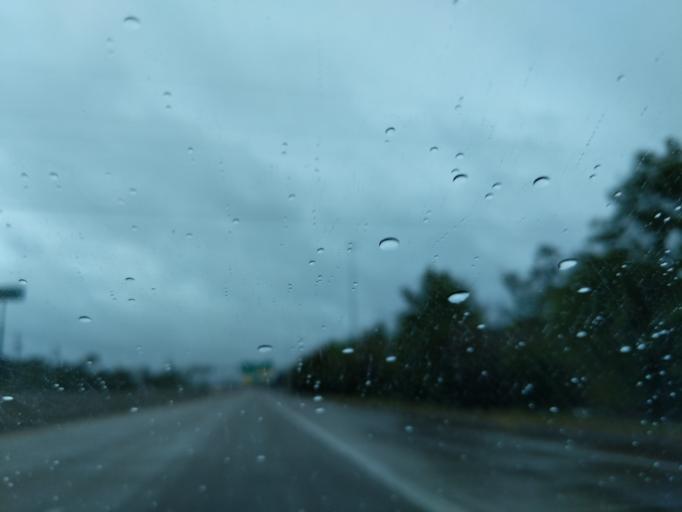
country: US
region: Texas
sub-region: Angelina County
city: Lufkin
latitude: 31.3009
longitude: -94.7272
